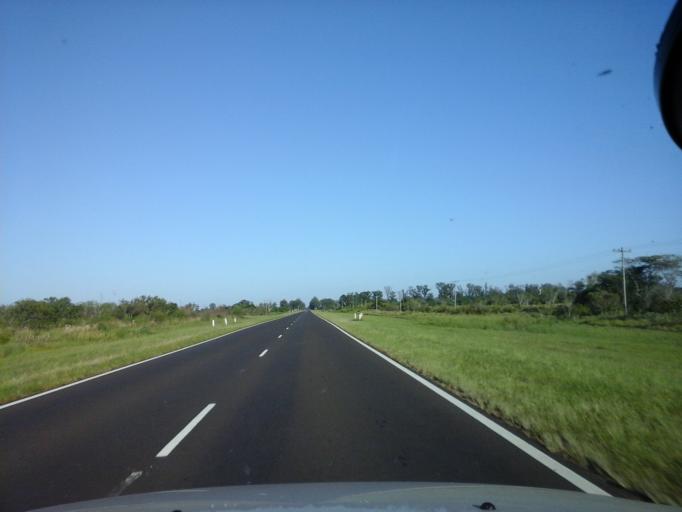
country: AR
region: Corrientes
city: Ita Ibate
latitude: -27.4649
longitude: -57.3106
